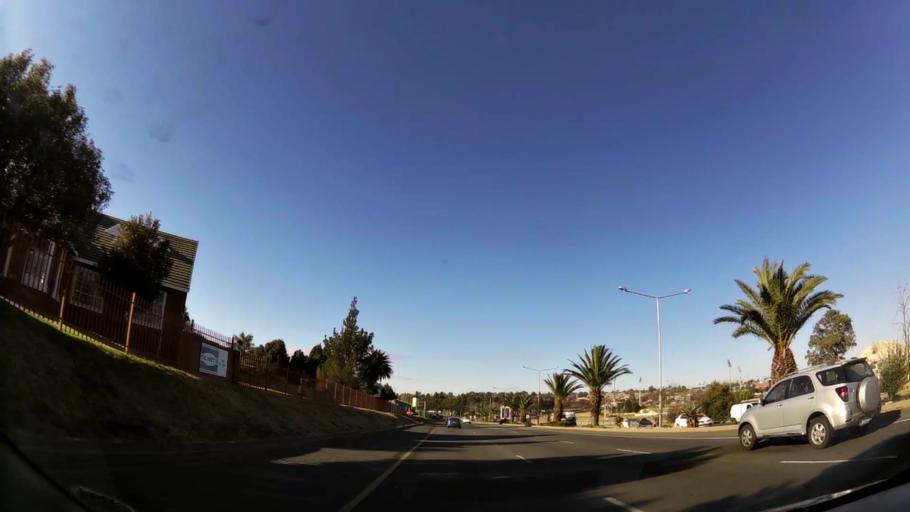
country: ZA
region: Gauteng
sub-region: West Rand District Municipality
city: Krugersdorp
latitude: -26.0968
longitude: 27.7788
